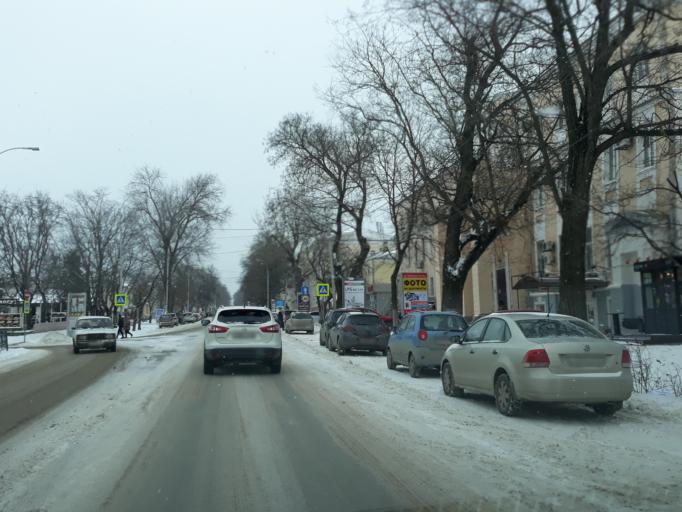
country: RU
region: Rostov
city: Taganrog
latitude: 47.2177
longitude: 38.9255
